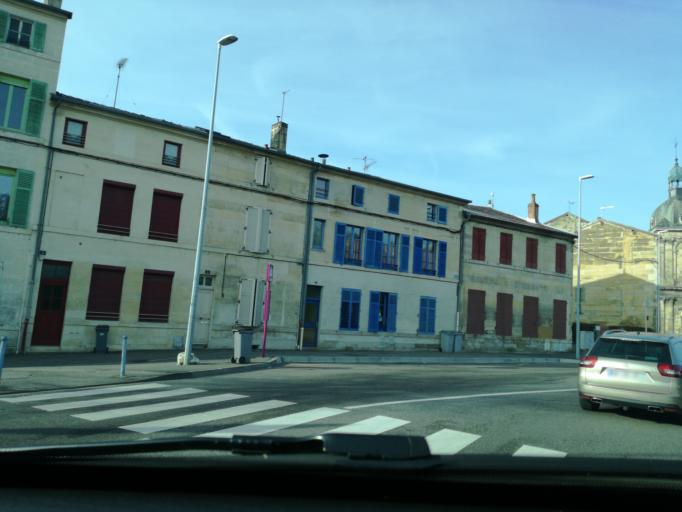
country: FR
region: Lorraine
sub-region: Departement de la Meuse
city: Bar-le-Duc
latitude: 48.7755
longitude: 5.1635
